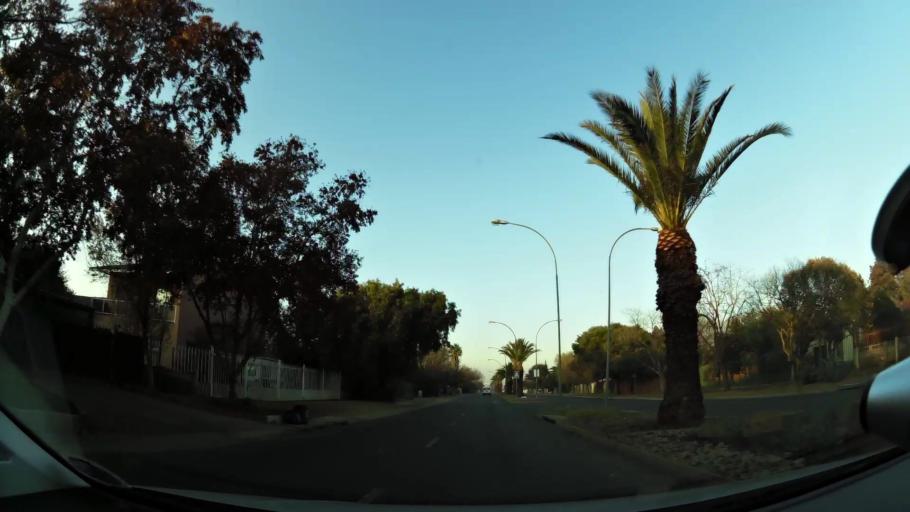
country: ZA
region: Orange Free State
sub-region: Mangaung Metropolitan Municipality
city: Bloemfontein
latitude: -29.1043
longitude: 26.1561
